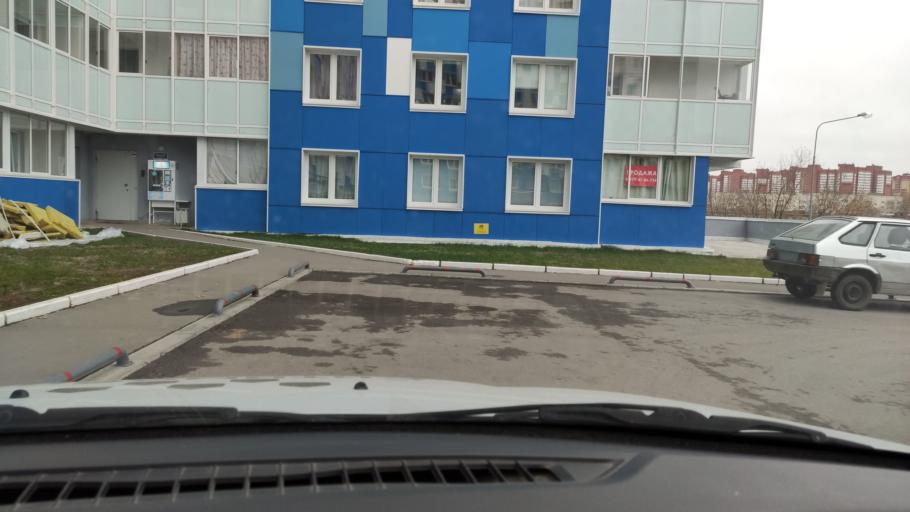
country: RU
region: Perm
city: Perm
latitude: 57.9899
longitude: 56.2681
